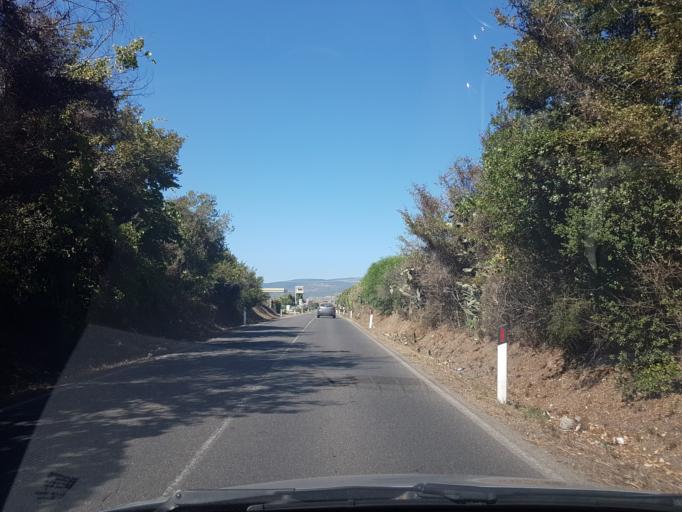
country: IT
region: Sardinia
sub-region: Provincia di Oristano
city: Nurachi
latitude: 39.9830
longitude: 8.5395
